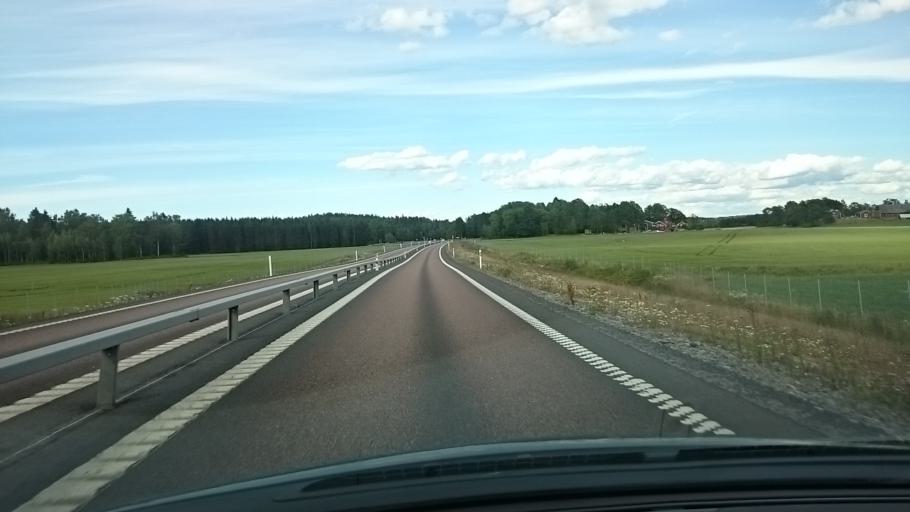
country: SE
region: OErebro
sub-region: Askersunds Kommun
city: Askersund
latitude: 58.8286
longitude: 14.8949
